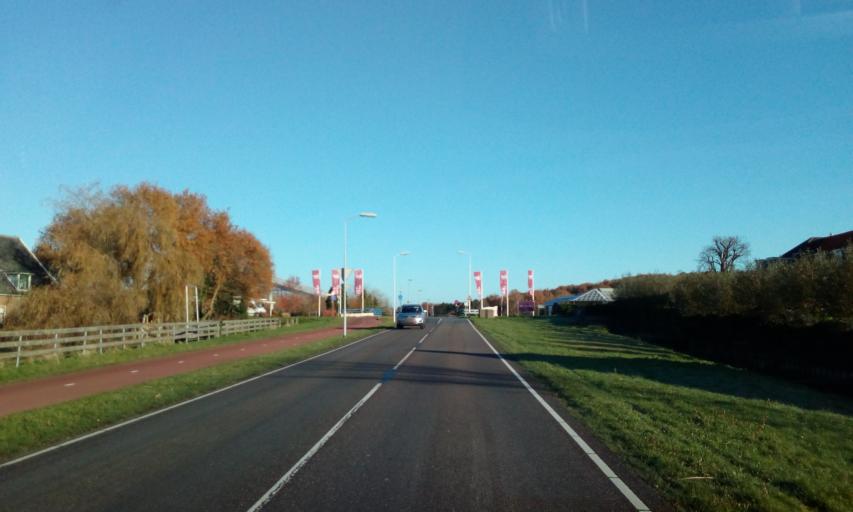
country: NL
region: South Holland
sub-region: Gemeente Zoetermeer
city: Zoetermeer
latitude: 52.0642
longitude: 4.4523
